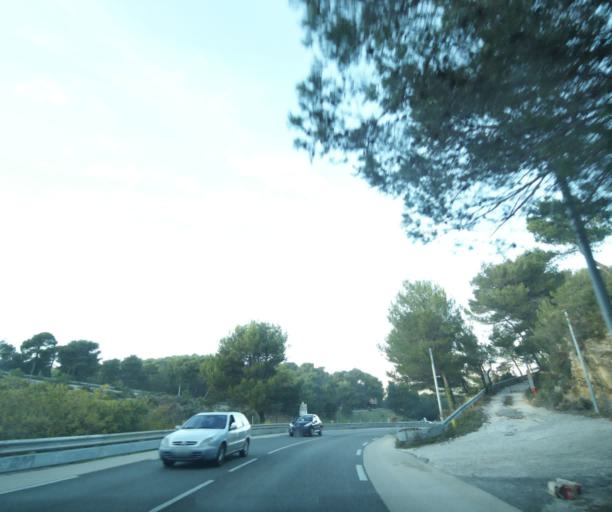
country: FR
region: Provence-Alpes-Cote d'Azur
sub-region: Departement des Bouches-du-Rhone
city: Roquefort-la-Bedoule
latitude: 43.2396
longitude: 5.5929
